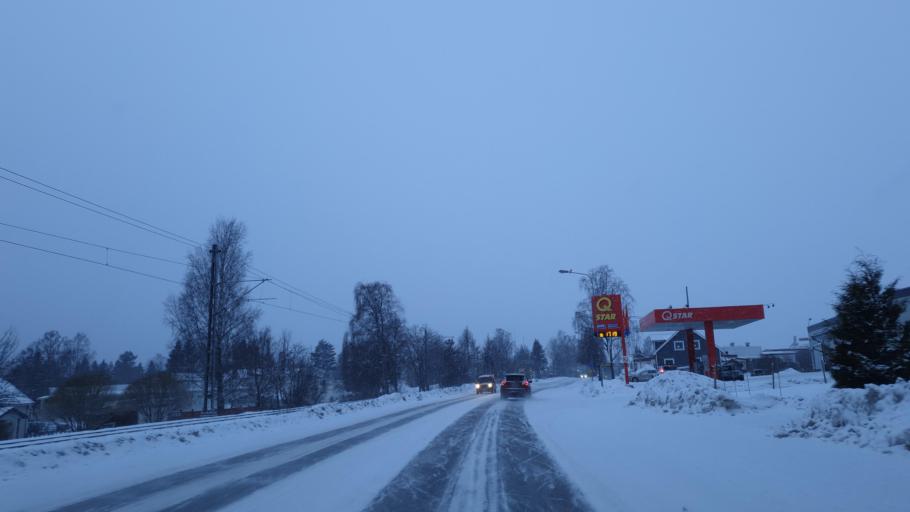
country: SE
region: Vaesternorrland
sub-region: OErnskoeldsviks Kommun
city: Ornskoldsvik
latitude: 63.2955
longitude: 18.6249
